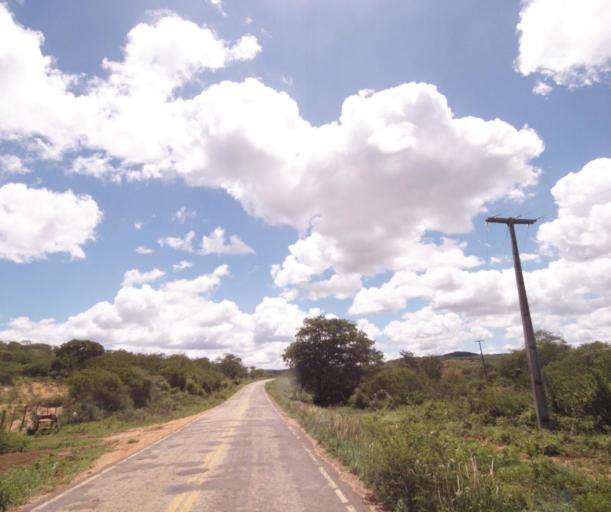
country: BR
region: Bahia
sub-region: Pocoes
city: Pocoes
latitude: -14.3853
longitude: -40.5158
